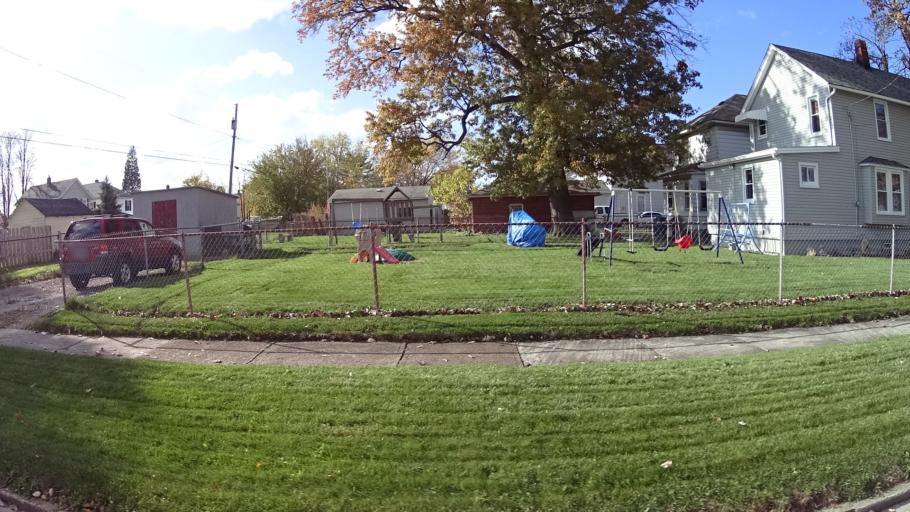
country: US
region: Ohio
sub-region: Lorain County
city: Sheffield
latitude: 41.4445
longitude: -82.1127
